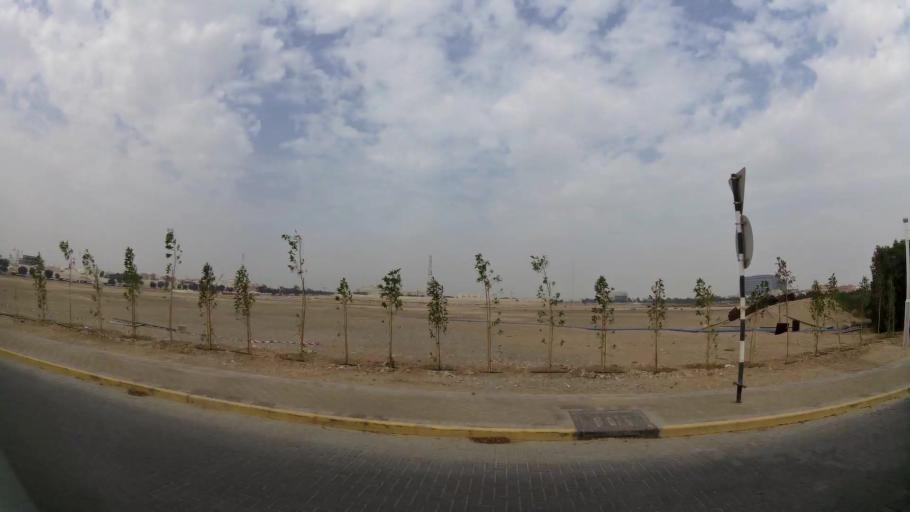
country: AE
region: Abu Dhabi
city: Abu Dhabi
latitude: 24.3119
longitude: 54.6177
